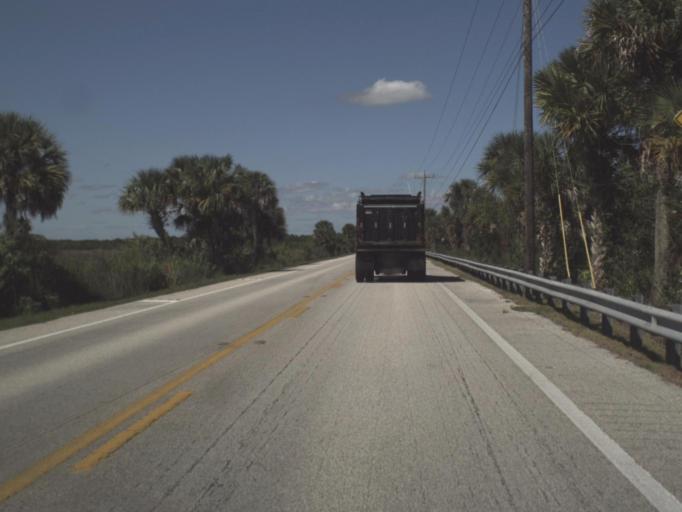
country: US
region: Florida
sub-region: Collier County
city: Marco
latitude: 25.9337
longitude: -81.4485
